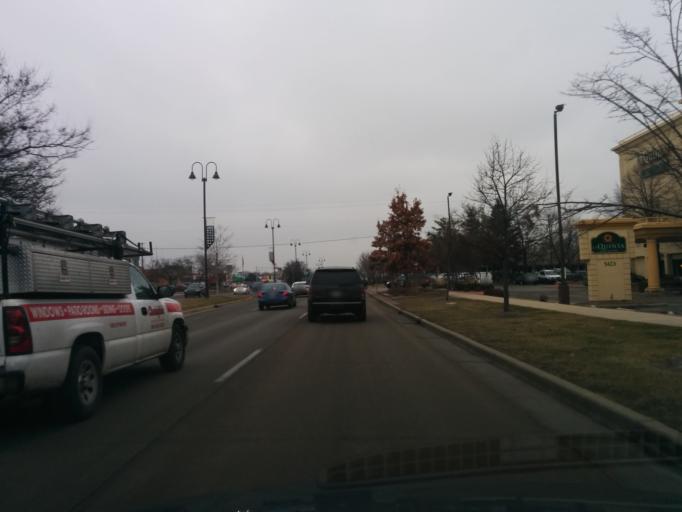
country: US
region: Wisconsin
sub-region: Milwaukee County
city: Whitefish Bay
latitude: 43.1157
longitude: -87.9168
